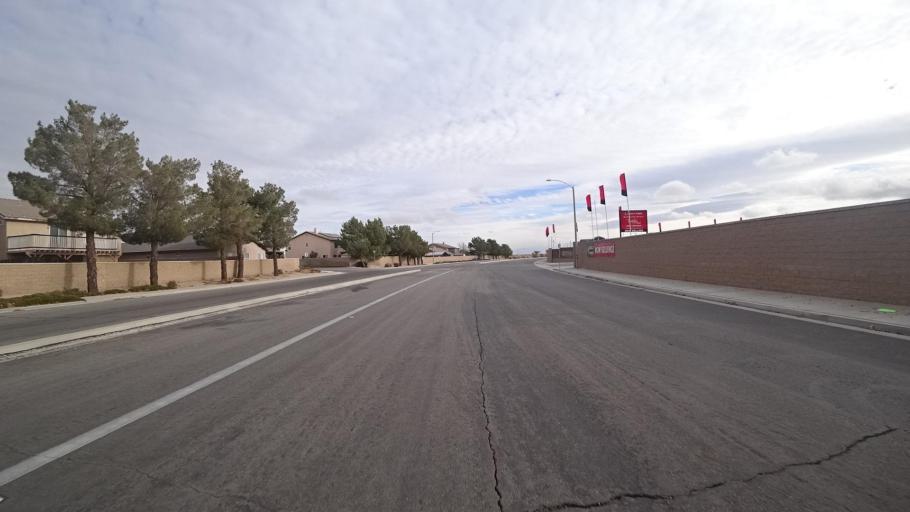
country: US
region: California
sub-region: Kern County
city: Rosamond
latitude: 34.8515
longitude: -118.1998
